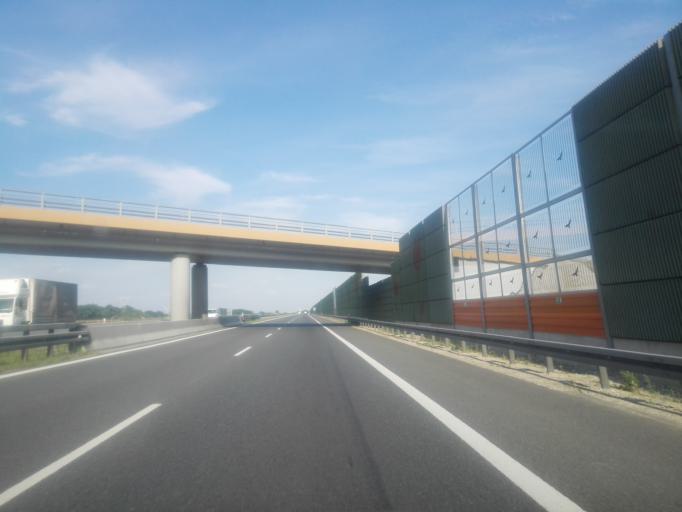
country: PL
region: Lower Silesian Voivodeship
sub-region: Powiat wroclawski
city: Dlugoleka
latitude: 51.2253
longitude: 17.1833
